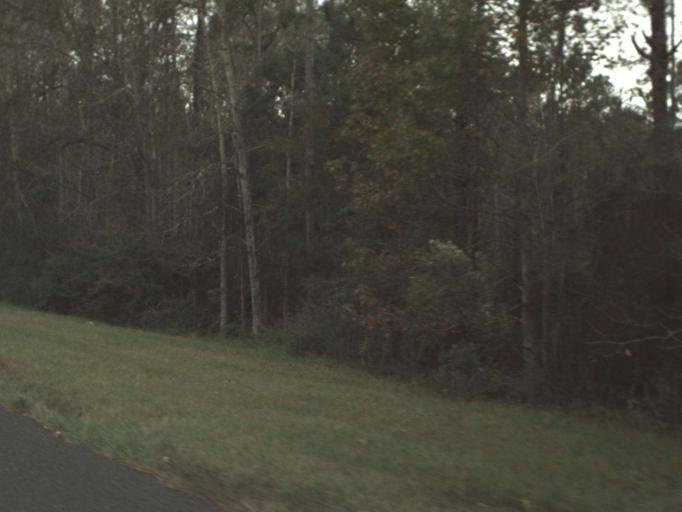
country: US
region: Florida
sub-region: Escambia County
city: Molino
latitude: 30.8159
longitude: -87.3350
